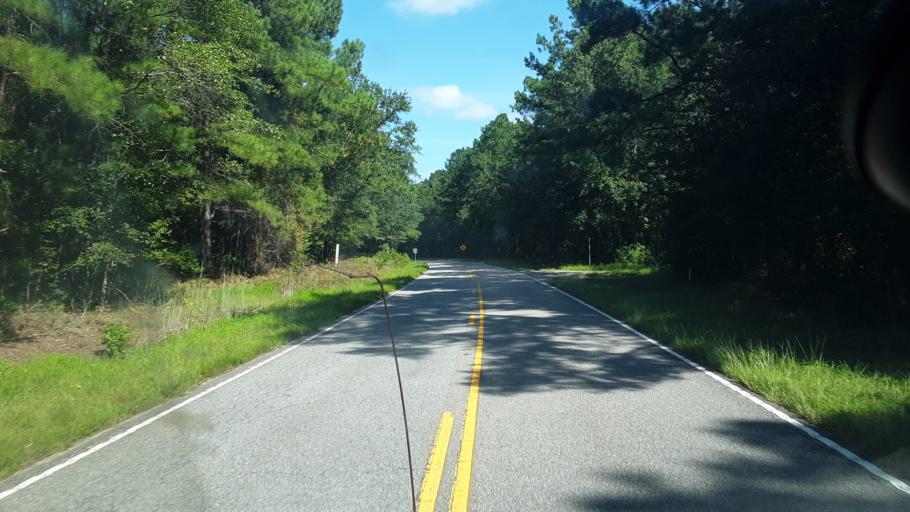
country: US
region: South Carolina
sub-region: Hampton County
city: Varnville
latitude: 32.7302
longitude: -81.0319
